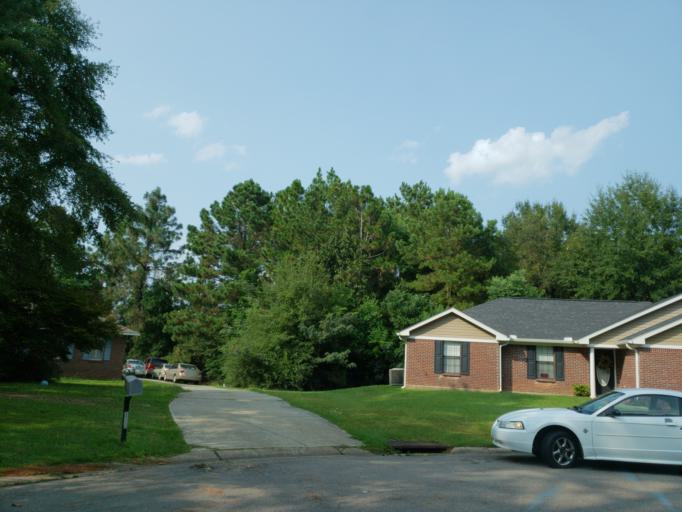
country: US
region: Mississippi
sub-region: Lamar County
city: West Hattiesburg
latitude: 31.3184
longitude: -89.3504
